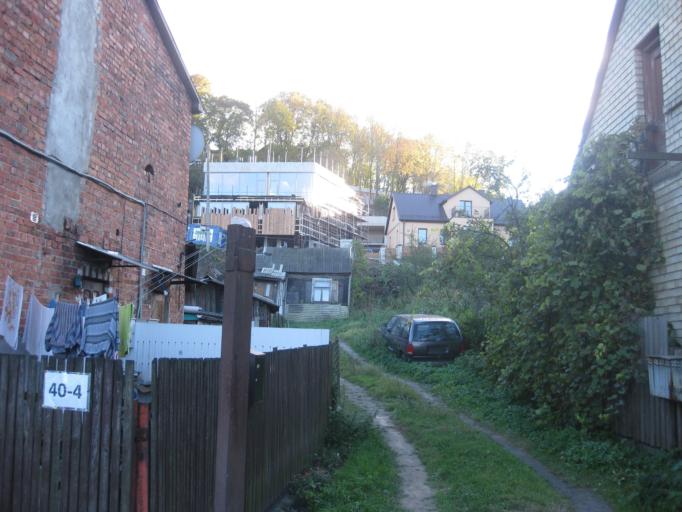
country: LT
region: Kauno apskritis
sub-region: Kaunas
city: Aleksotas
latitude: 54.8917
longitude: 23.8946
